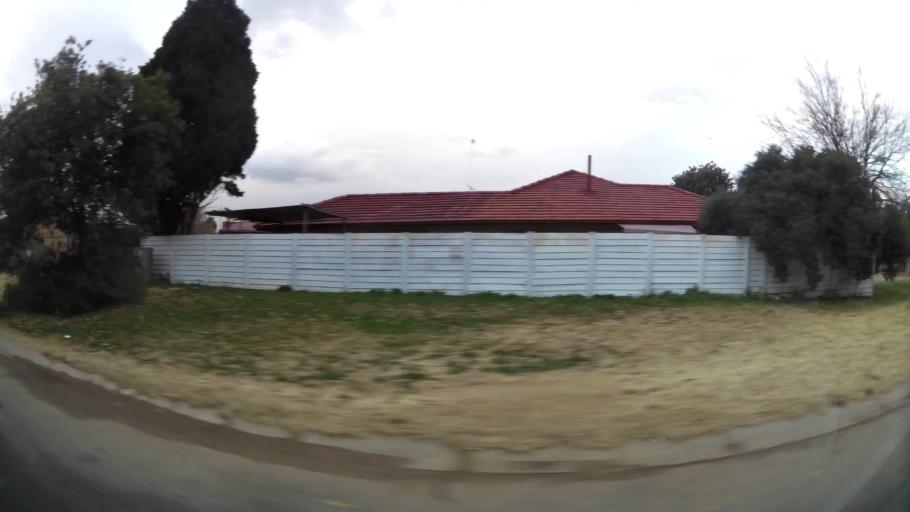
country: ZA
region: Orange Free State
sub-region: Lejweleputswa District Municipality
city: Welkom
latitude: -27.9656
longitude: 26.7404
